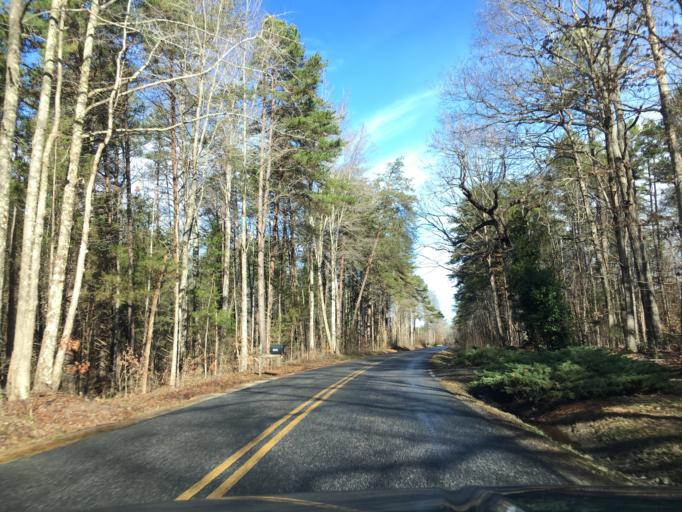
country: US
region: Virginia
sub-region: Cumberland County
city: Cumberland
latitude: 37.3527
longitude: -78.1562
